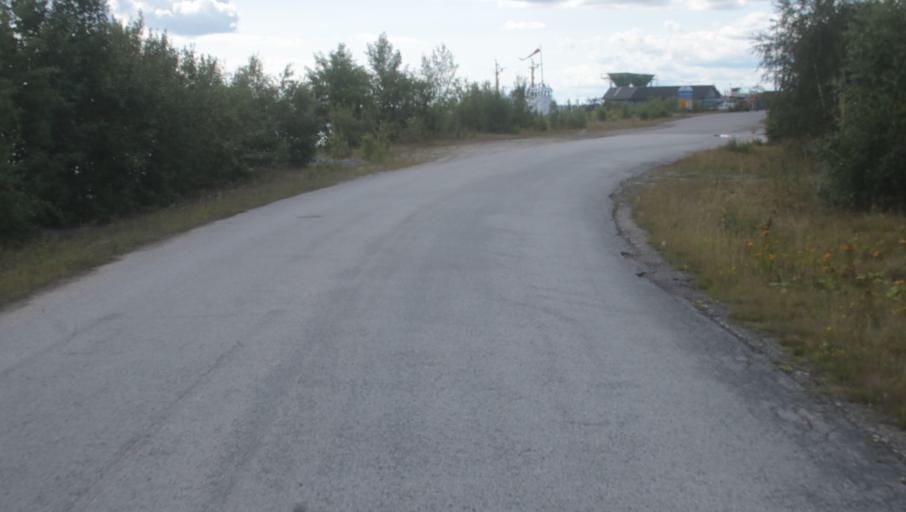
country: SE
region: Blekinge
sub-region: Karlshamns Kommun
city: Karlshamn
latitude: 56.1577
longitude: 14.8316
